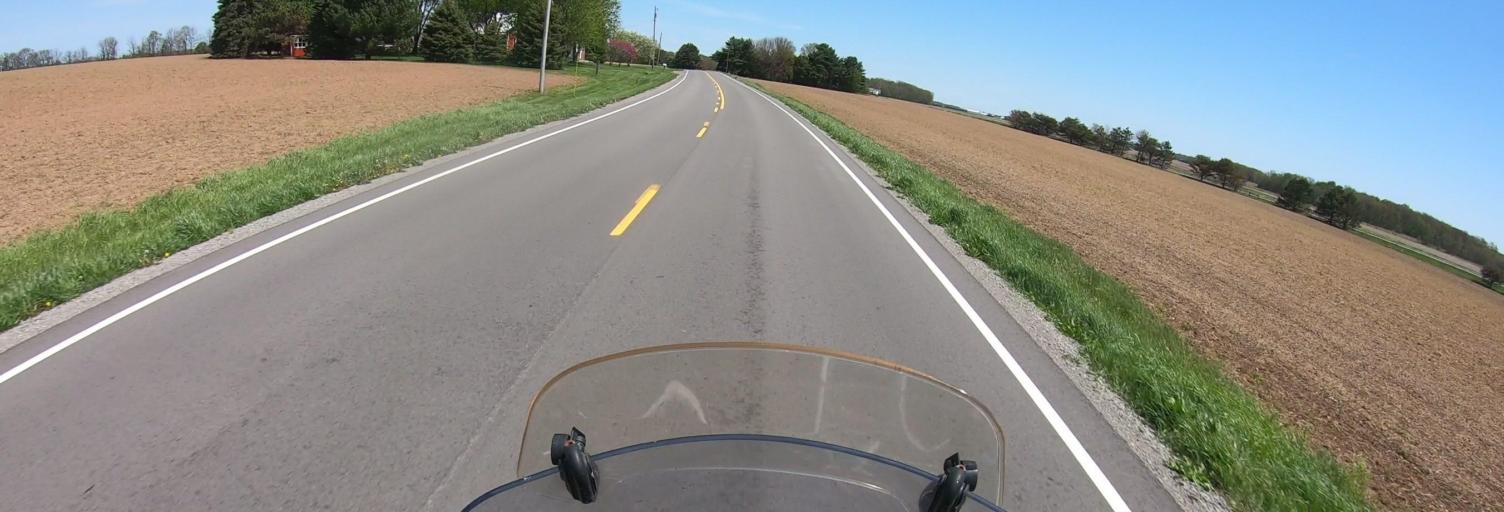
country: US
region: Ohio
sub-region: Allen County
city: Bluffton
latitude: 40.9110
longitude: -83.8475
